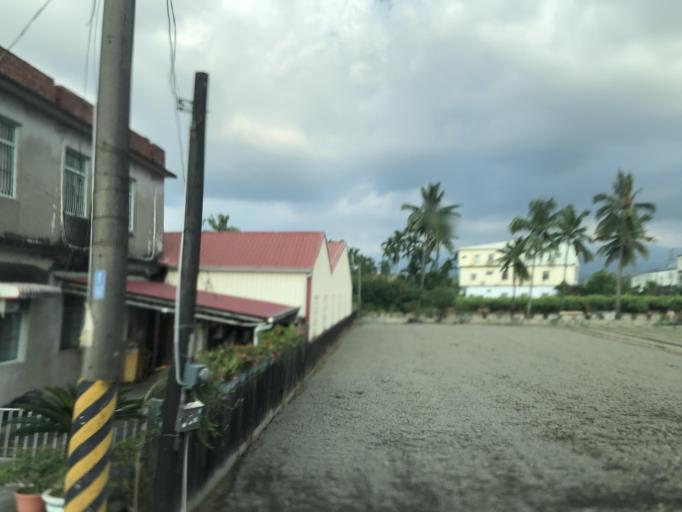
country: TW
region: Taiwan
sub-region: Pingtung
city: Pingtung
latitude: 22.8730
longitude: 120.5365
